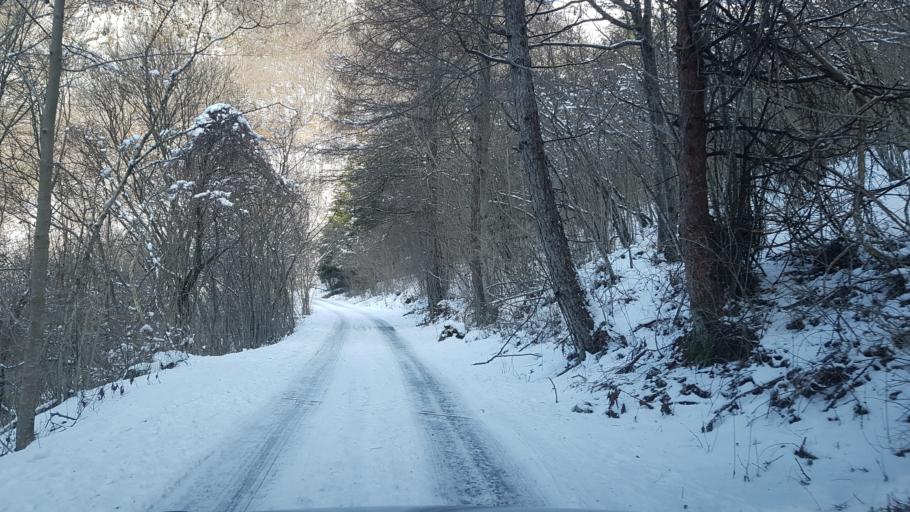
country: IT
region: Friuli Venezia Giulia
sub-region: Provincia di Udine
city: Montenars
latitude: 46.2770
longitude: 13.1618
